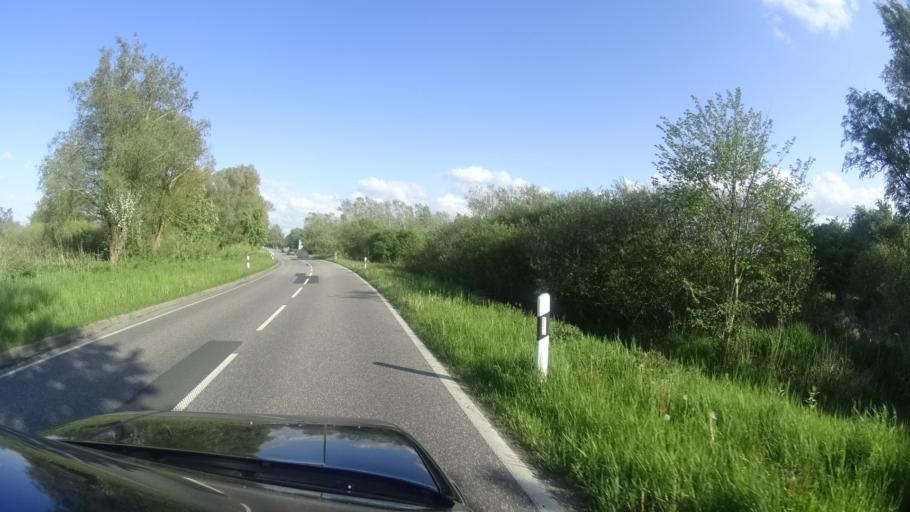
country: DE
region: Mecklenburg-Vorpommern
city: Ostseebad Dierhagen
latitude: 54.2511
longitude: 12.3930
